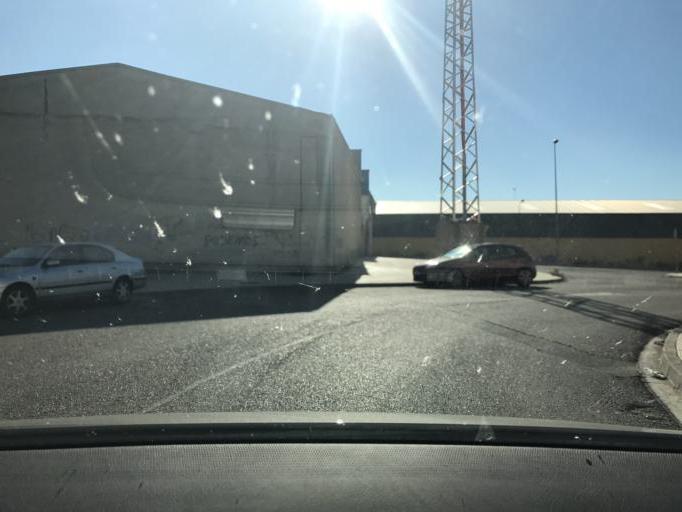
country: ES
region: Andalusia
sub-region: Provincia de Granada
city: Peligros
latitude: 37.2257
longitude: -3.6306
